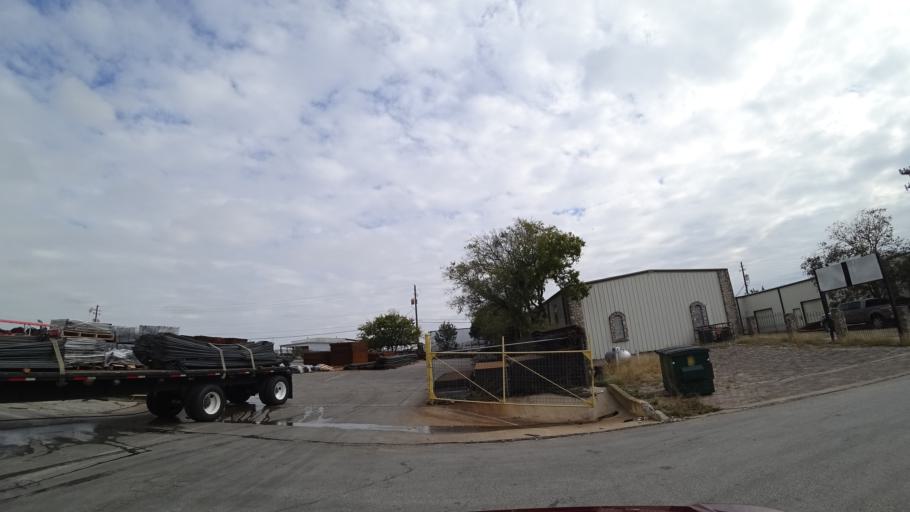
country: US
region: Texas
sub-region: Travis County
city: Wells Branch
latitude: 30.4328
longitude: -97.6836
